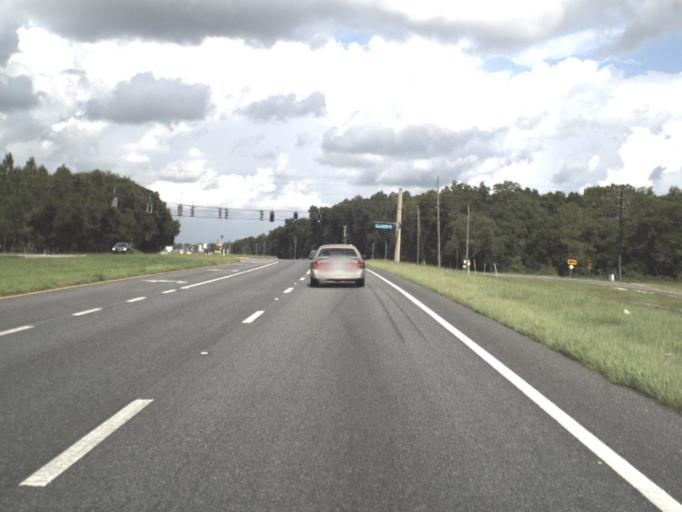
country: US
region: Florida
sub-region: Hernando County
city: Ridge Manor
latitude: 28.5229
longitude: -82.2188
